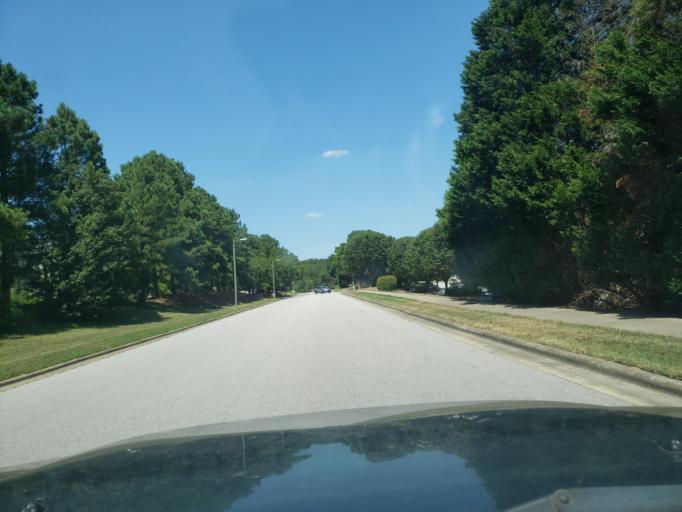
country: US
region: North Carolina
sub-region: Durham County
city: Durham
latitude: 35.9091
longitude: -78.9480
